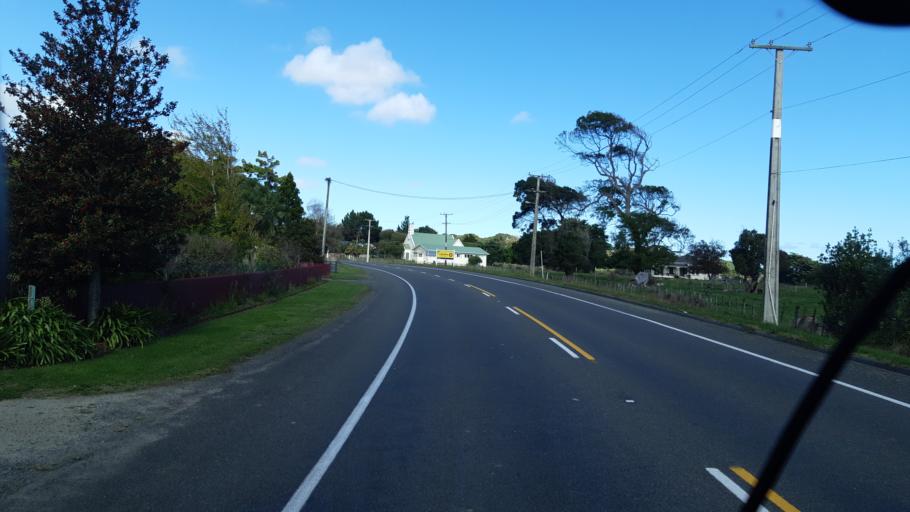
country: NZ
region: Manawatu-Wanganui
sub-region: Wanganui District
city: Wanganui
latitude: -40.0426
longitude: 175.2120
